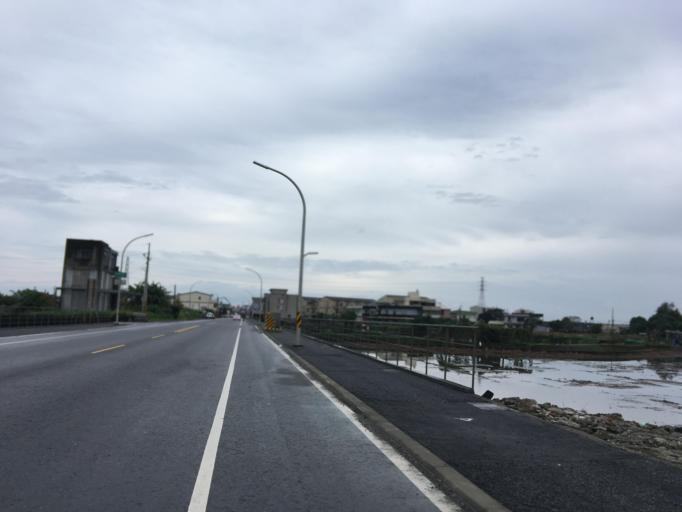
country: TW
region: Taiwan
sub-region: Yilan
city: Yilan
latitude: 24.6372
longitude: 121.7968
